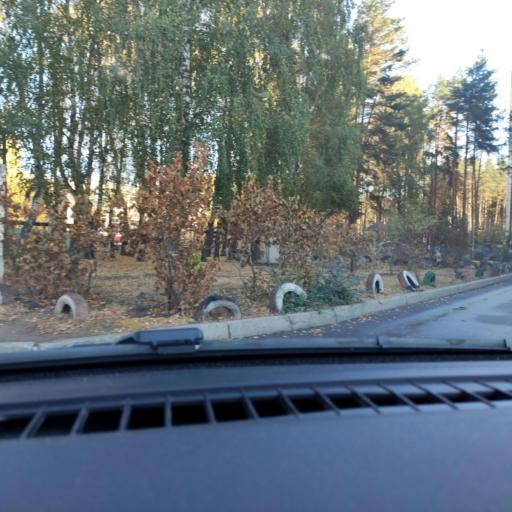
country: RU
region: Voronezj
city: Pridonskoy
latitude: 51.6818
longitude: 39.0911
